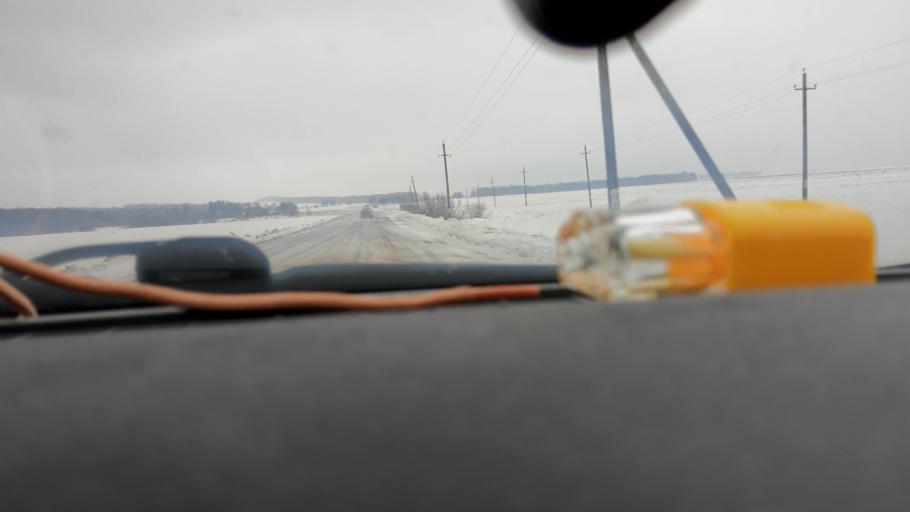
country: RU
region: Bashkortostan
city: Ulukulevo
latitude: 54.5982
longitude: 56.4269
